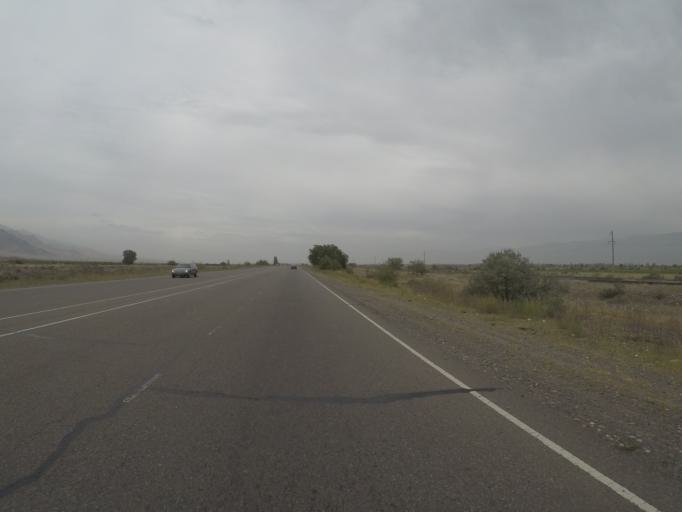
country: KG
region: Chuy
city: Tokmok
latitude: 42.8314
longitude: 75.4544
